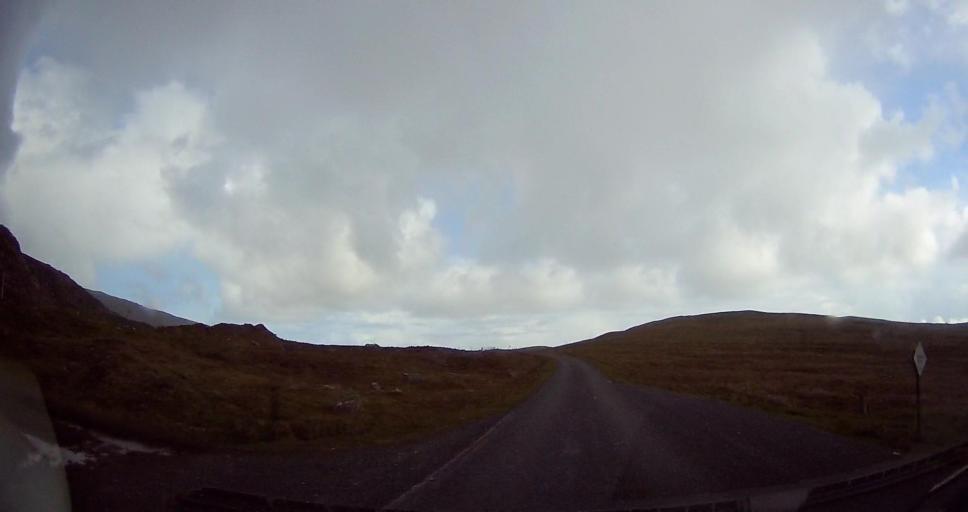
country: GB
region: Scotland
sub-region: Shetland Islands
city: Lerwick
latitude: 60.5525
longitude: -1.3411
